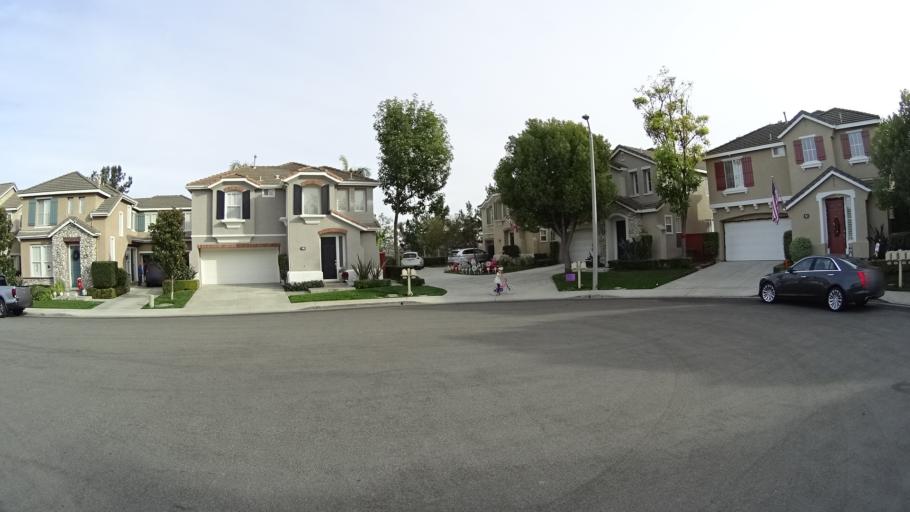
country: US
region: California
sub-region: Orange County
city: Aliso Viejo
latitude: 33.5747
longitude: -117.7316
